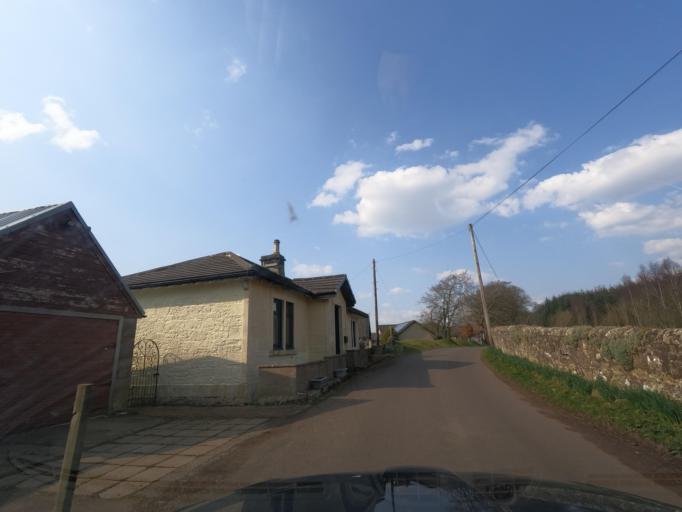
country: GB
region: Scotland
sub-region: South Lanarkshire
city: Carnwath
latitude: 55.7375
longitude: -3.6119
